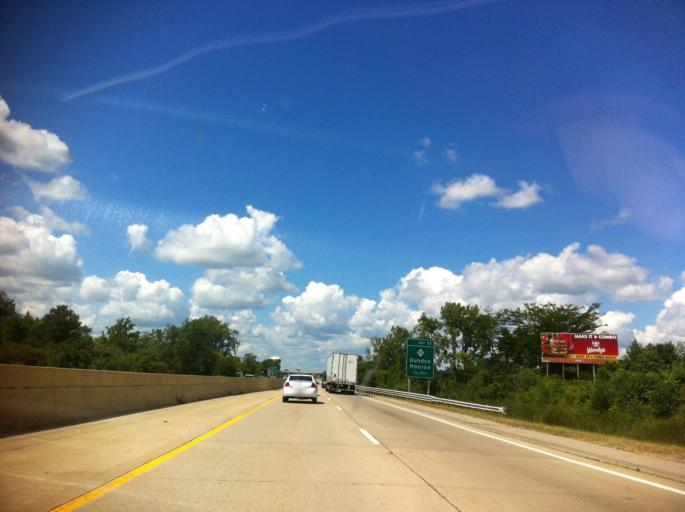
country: US
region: Michigan
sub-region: Monroe County
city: Dundee
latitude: 41.9449
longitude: -83.6653
